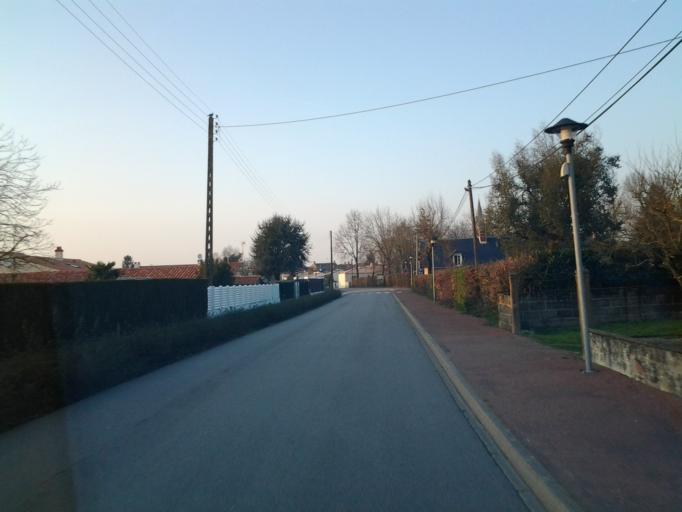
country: FR
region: Pays de la Loire
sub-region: Departement de la Vendee
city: La Chaize-le-Vicomte
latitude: 46.6563
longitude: -1.2314
